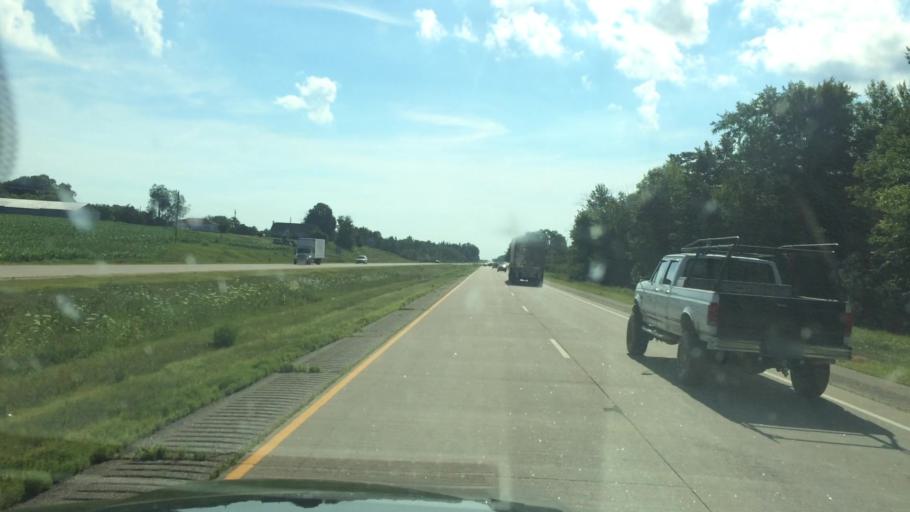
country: US
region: Wisconsin
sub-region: Waupaca County
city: Marion
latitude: 44.8041
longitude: -88.9680
